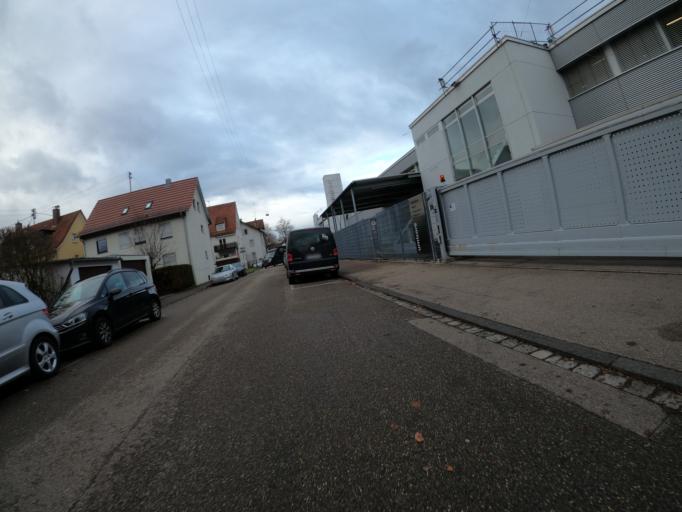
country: DE
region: Baden-Wuerttemberg
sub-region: Regierungsbezirk Stuttgart
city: Schwabisch Gmund
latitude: 48.7933
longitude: 9.8086
